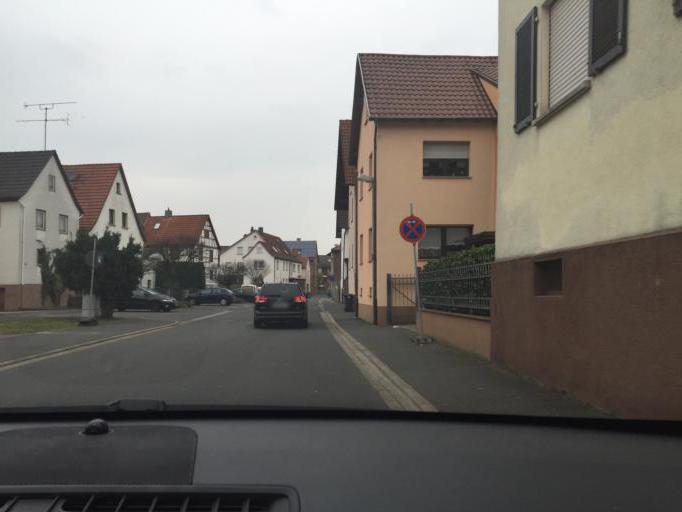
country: DE
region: Bavaria
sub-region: Regierungsbezirk Unterfranken
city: Hosbach
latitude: 50.0013
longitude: 9.2016
